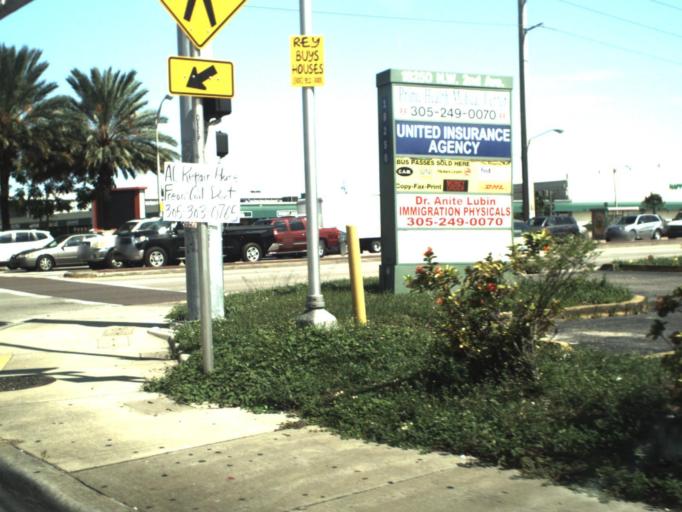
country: US
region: Florida
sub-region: Miami-Dade County
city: Norland
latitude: 25.9424
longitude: -80.2055
